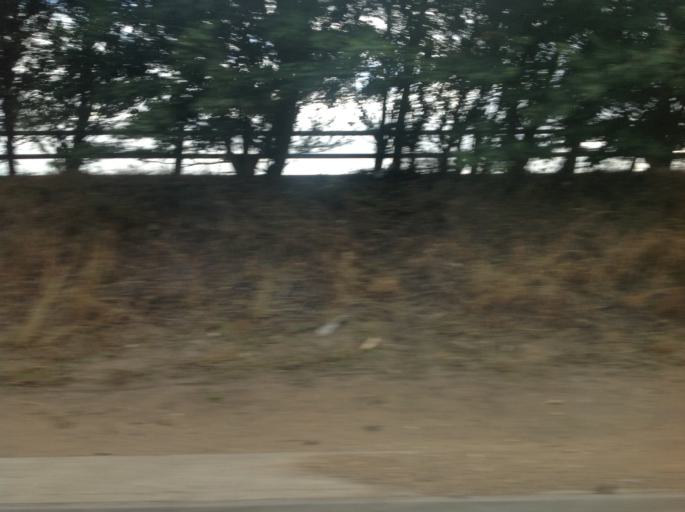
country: GB
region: England
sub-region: Suffolk
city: Shotley Gate
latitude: 52.0157
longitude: 1.2729
